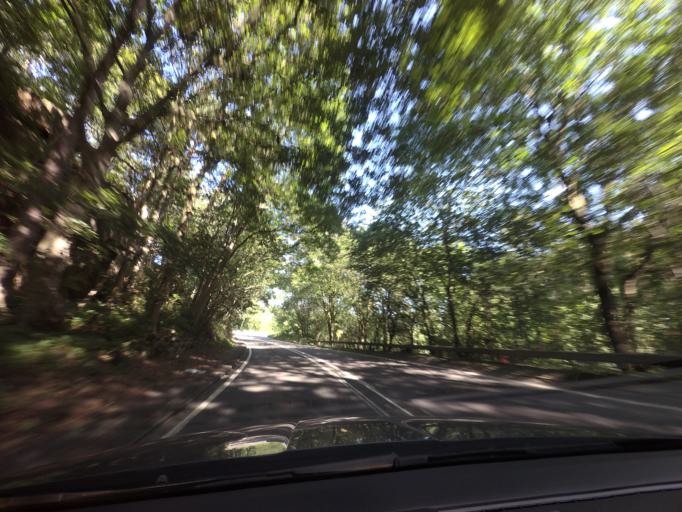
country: GB
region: England
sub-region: Derbyshire
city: Bakewell
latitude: 53.2457
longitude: -1.5884
